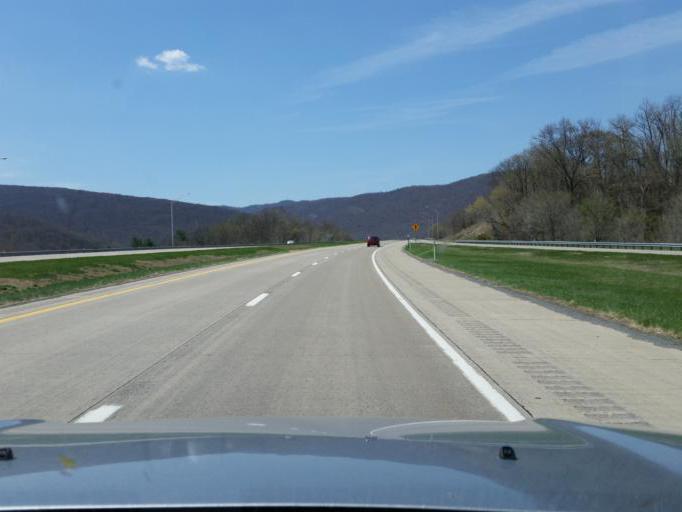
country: US
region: Pennsylvania
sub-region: Juniata County
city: Mifflintown
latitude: 40.6017
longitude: -77.4193
